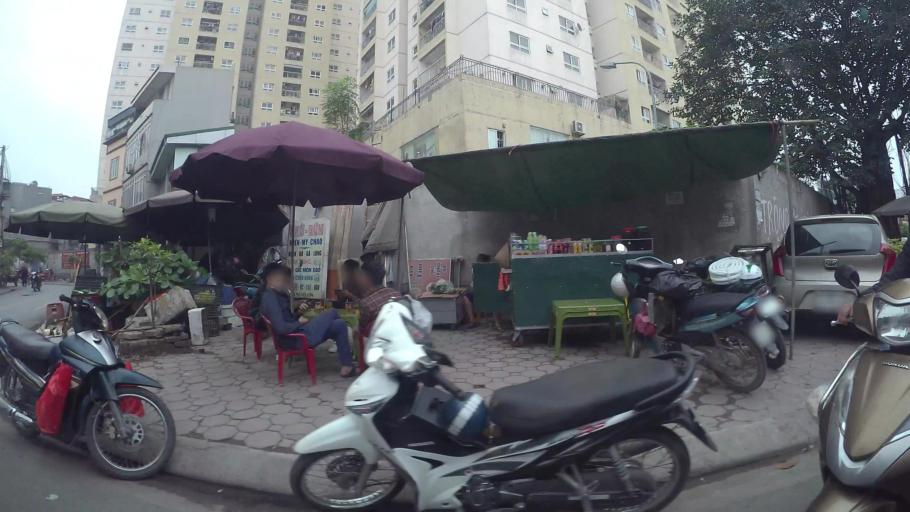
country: VN
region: Ha Noi
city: Hai BaTrung
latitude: 20.9934
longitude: 105.8570
